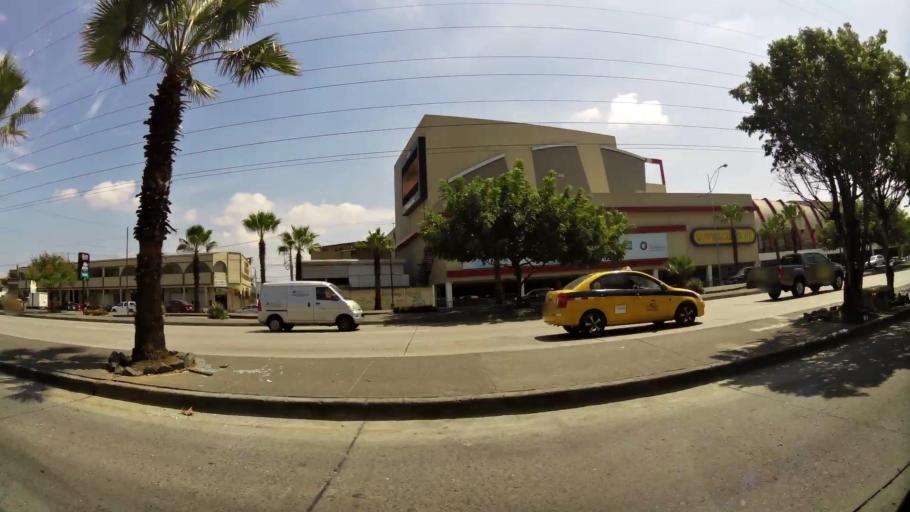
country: EC
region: Guayas
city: Eloy Alfaro
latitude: -2.1290
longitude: -79.9060
